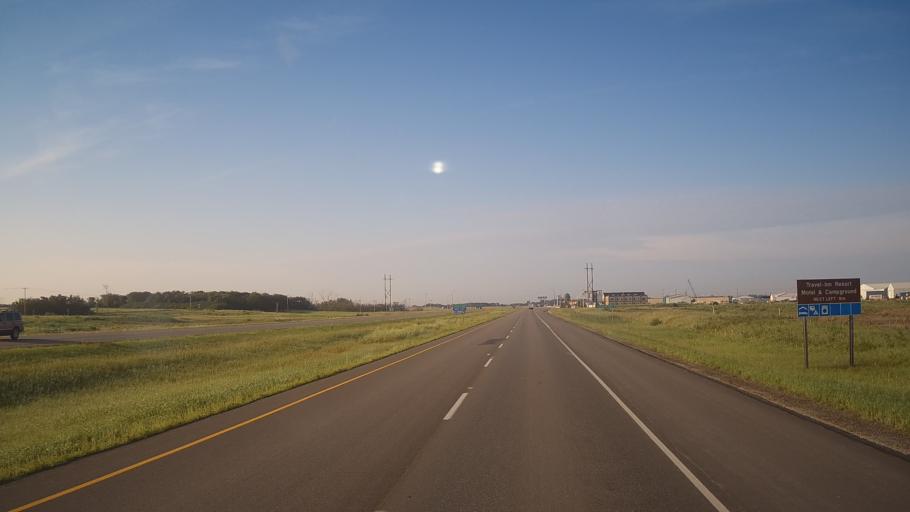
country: CA
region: Saskatchewan
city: Saskatoon
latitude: 52.0638
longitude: -106.6018
